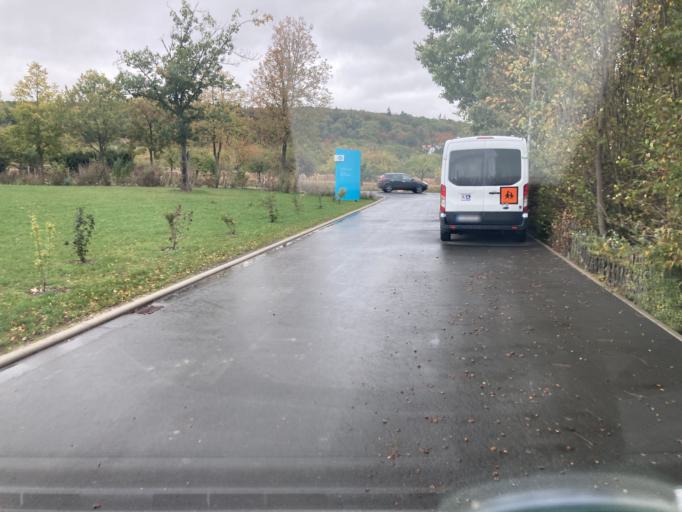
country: DE
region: Hesse
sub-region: Regierungsbezirk Darmstadt
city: Usingen
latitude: 50.3573
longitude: 8.5647
